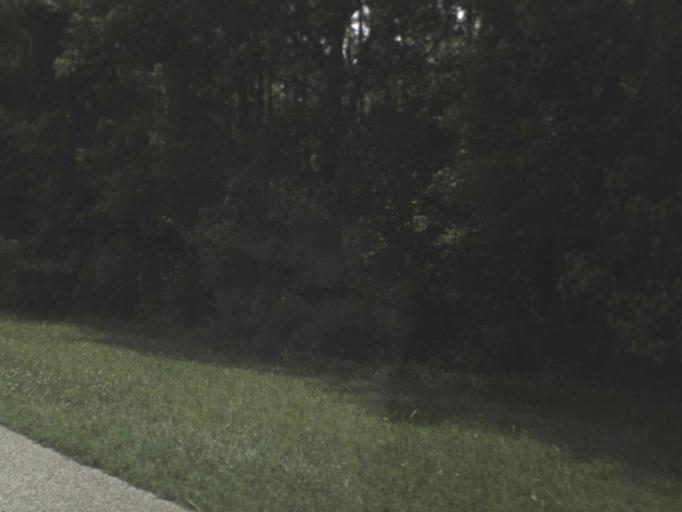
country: US
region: Florida
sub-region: Nassau County
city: Nassau Village-Ratliff
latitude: 30.4697
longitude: -81.7785
